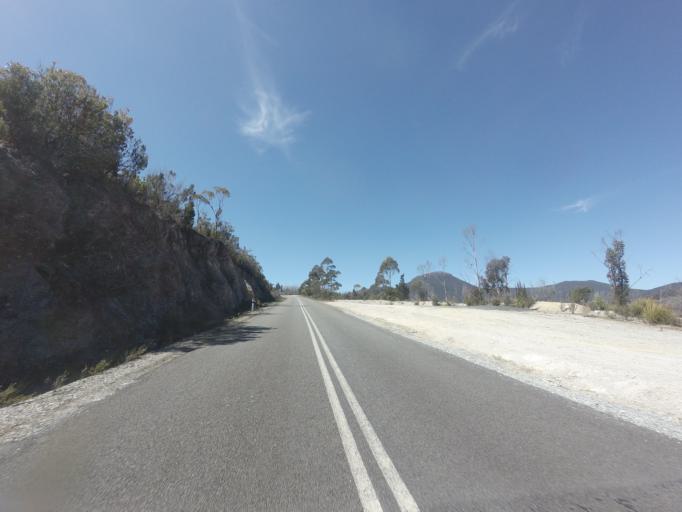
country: AU
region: Tasmania
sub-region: Huon Valley
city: Geeveston
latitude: -42.8554
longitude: 146.2339
